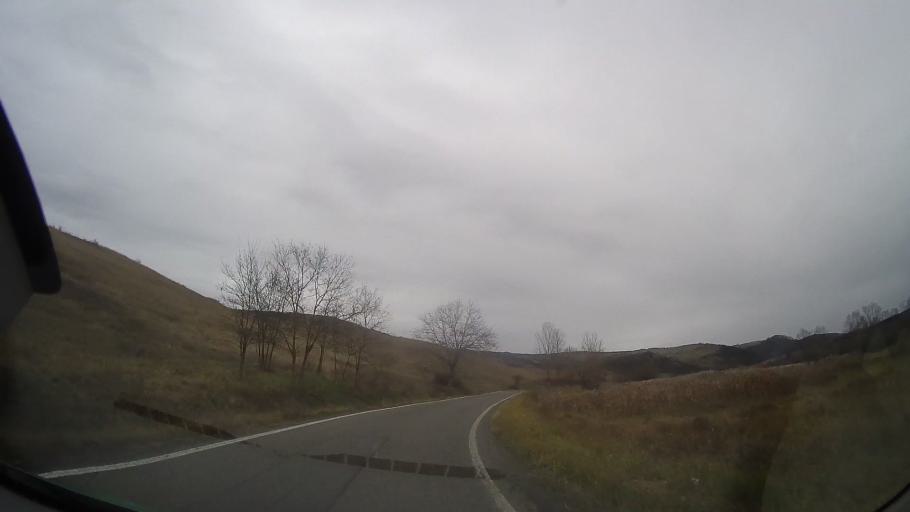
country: RO
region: Mures
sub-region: Comuna Bala
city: Bala
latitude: 46.7169
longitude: 24.5445
